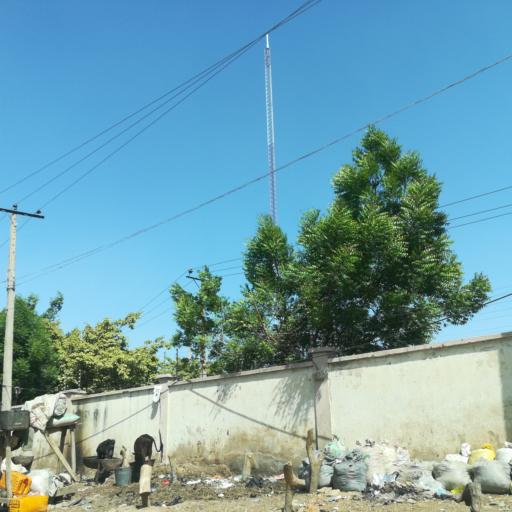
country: NG
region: Kano
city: Kano
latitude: 11.9931
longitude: 8.5311
